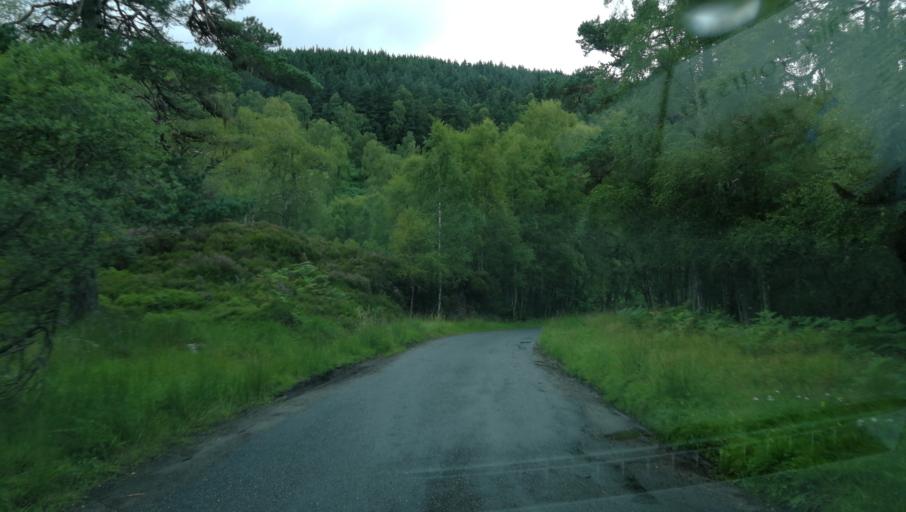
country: GB
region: Scotland
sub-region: Highland
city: Spean Bridge
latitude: 57.2929
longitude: -4.9176
